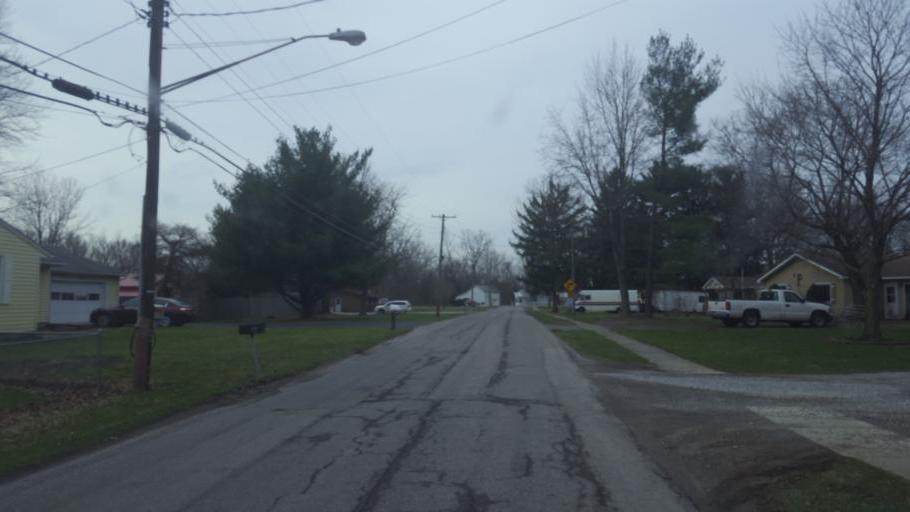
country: US
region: Ohio
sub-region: Morrow County
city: Cardington
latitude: 40.6411
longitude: -82.9660
